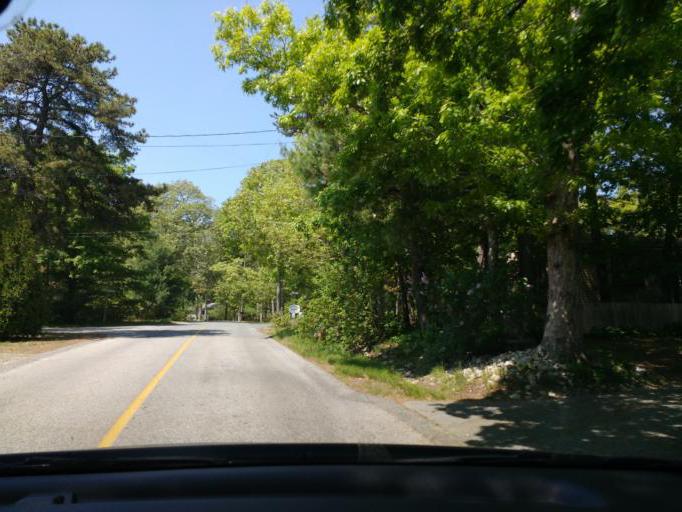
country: US
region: Massachusetts
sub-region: Barnstable County
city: East Falmouth
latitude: 41.6000
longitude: -70.5860
